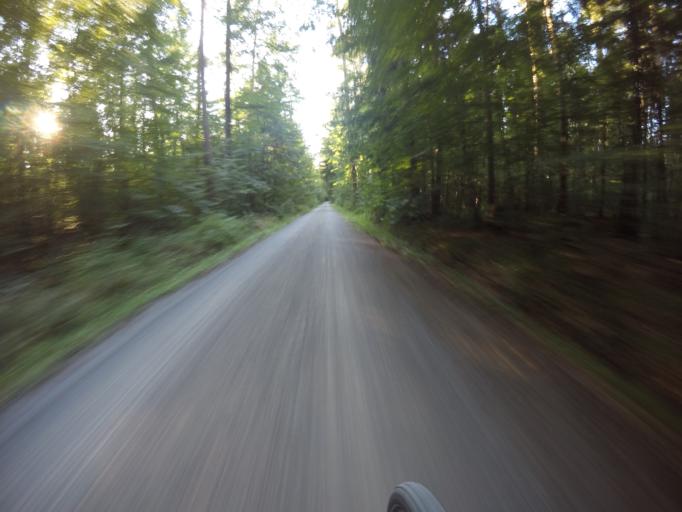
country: DE
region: Baden-Wuerttemberg
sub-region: Tuebingen Region
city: Dettenhausen
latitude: 48.6339
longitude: 9.0950
